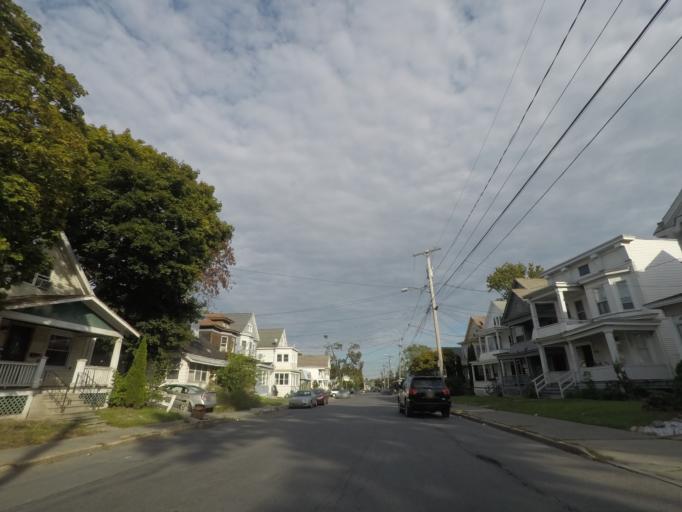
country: US
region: New York
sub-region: Albany County
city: Albany
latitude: 42.6394
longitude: -73.7816
